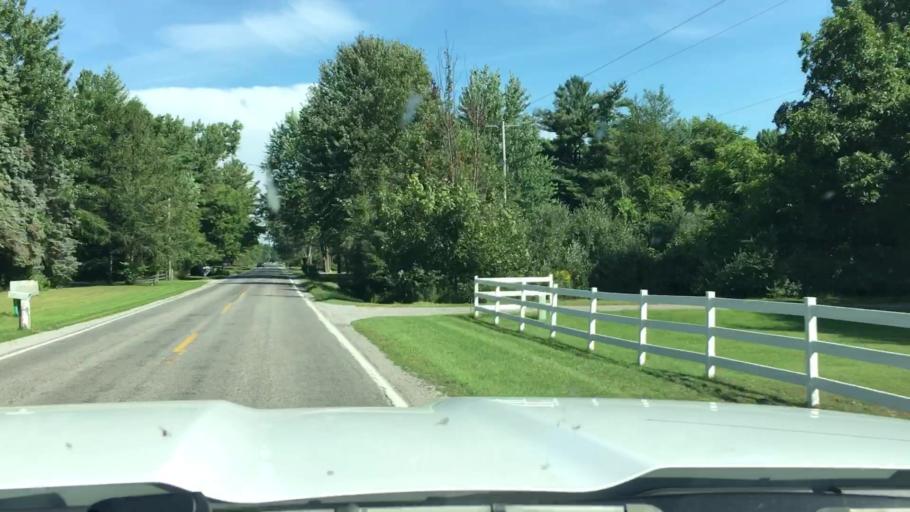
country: US
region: Michigan
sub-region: Saginaw County
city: Hemlock
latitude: 43.4717
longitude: -84.2303
